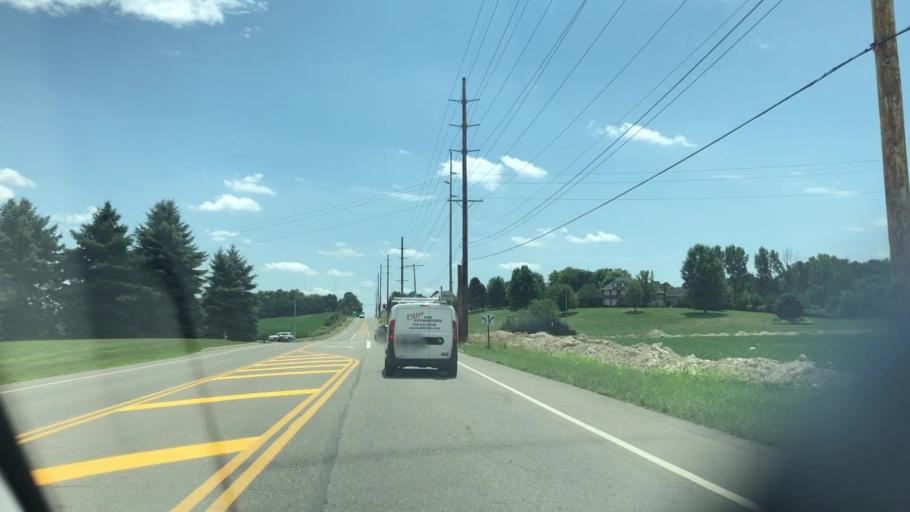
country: US
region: Ohio
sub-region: Summit County
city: Greensburg
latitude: 40.8810
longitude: -81.4994
